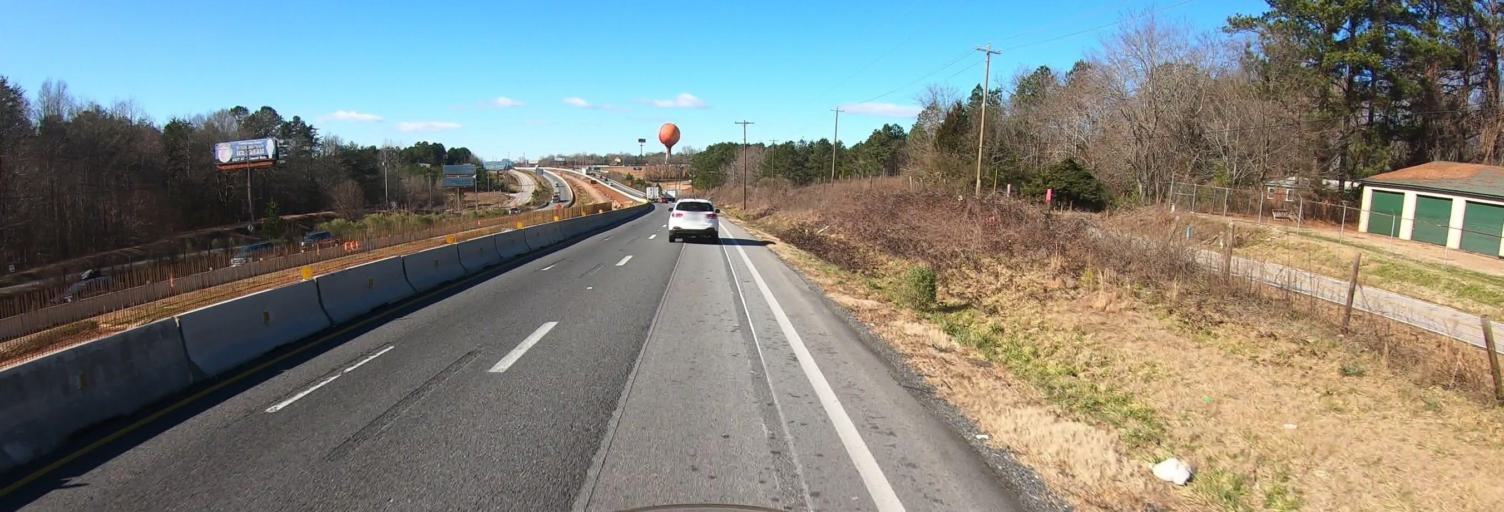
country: US
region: South Carolina
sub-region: Cherokee County
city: Gaffney
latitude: 35.0977
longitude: -81.6777
